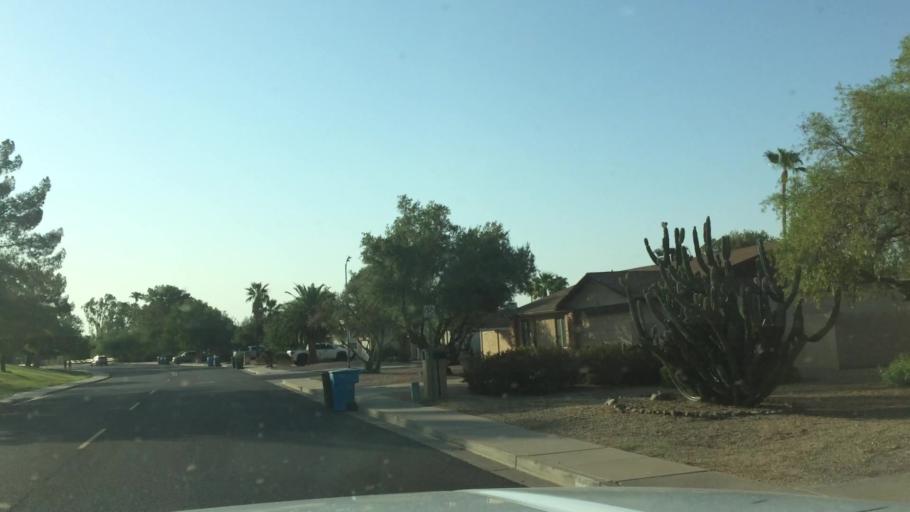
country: US
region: Arizona
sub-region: Maricopa County
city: Paradise Valley
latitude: 33.6192
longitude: -111.9493
